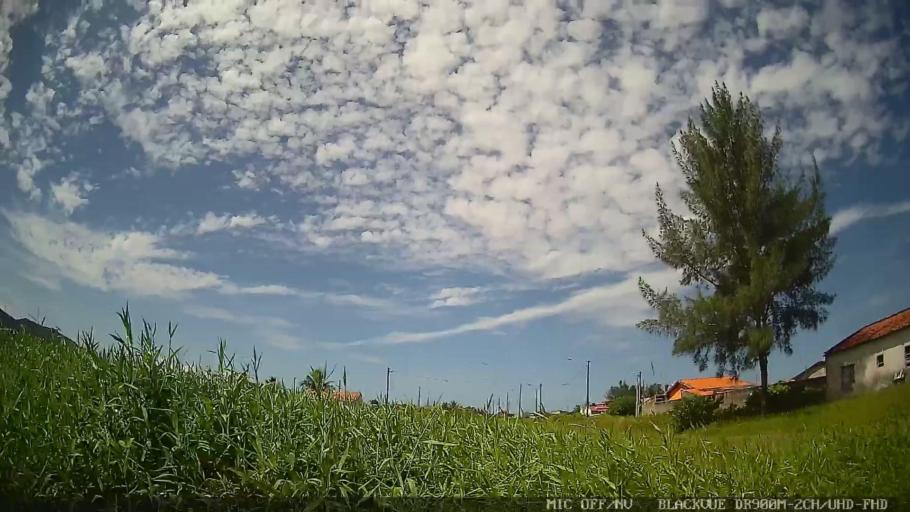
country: BR
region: Sao Paulo
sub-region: Iguape
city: Iguape
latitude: -24.7190
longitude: -47.5030
